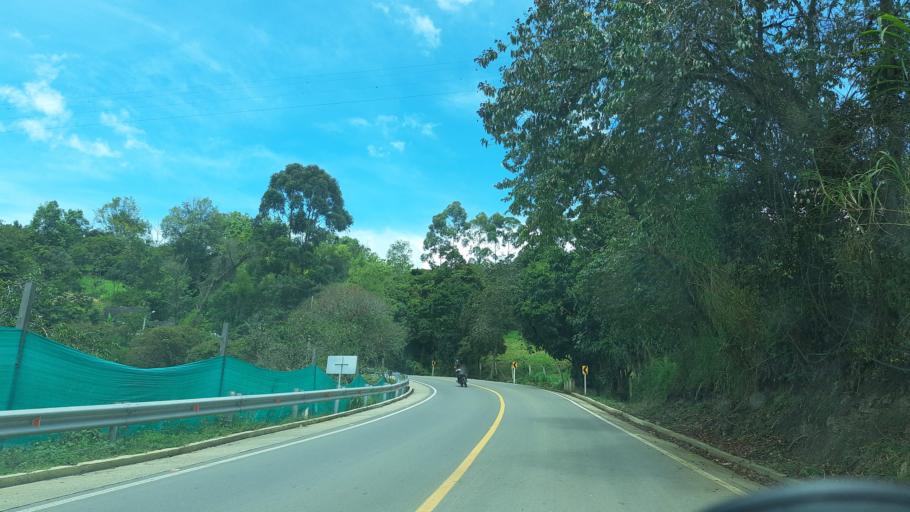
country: CO
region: Boyaca
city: Guateque
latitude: 5.0093
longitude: -73.4662
